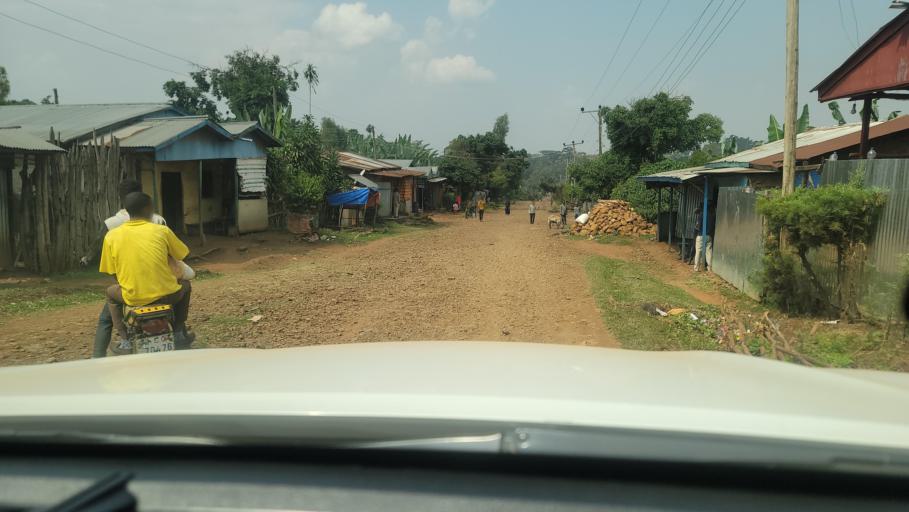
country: ET
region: Oromiya
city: Agaro
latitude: 7.8086
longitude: 36.4697
